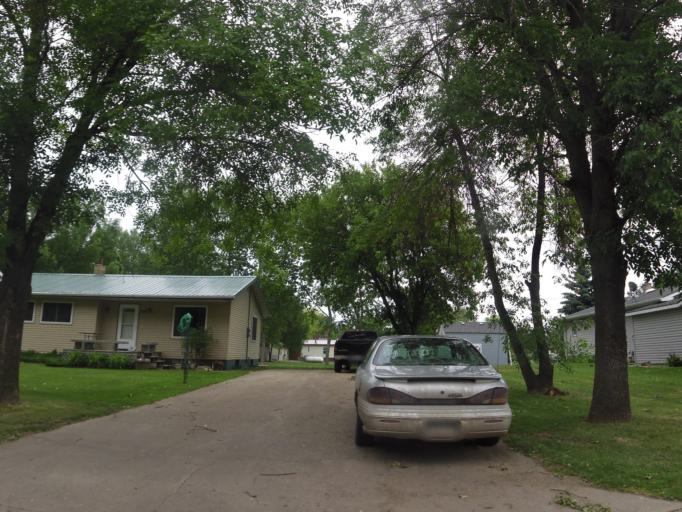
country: US
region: North Dakota
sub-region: Walsh County
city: Grafton
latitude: 48.6174
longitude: -97.4521
